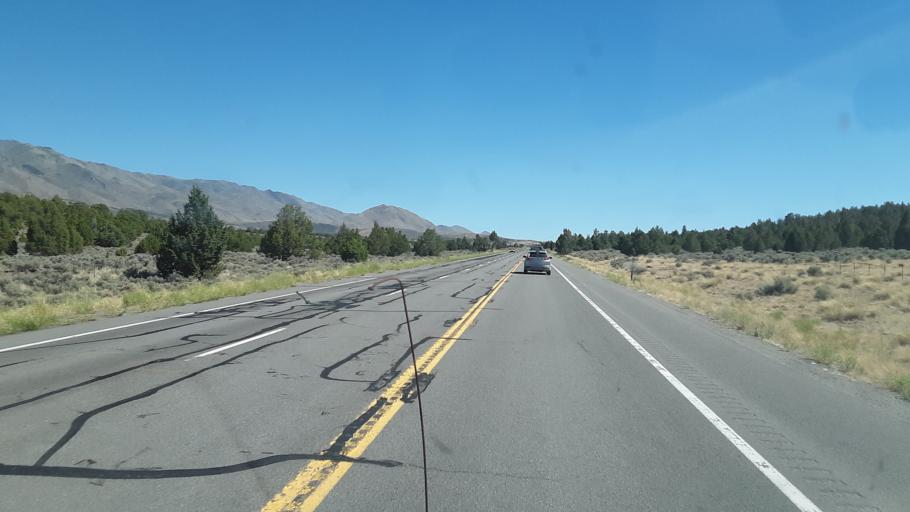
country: US
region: Nevada
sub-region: Washoe County
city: Cold Springs
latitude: 39.8424
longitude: -120.0398
